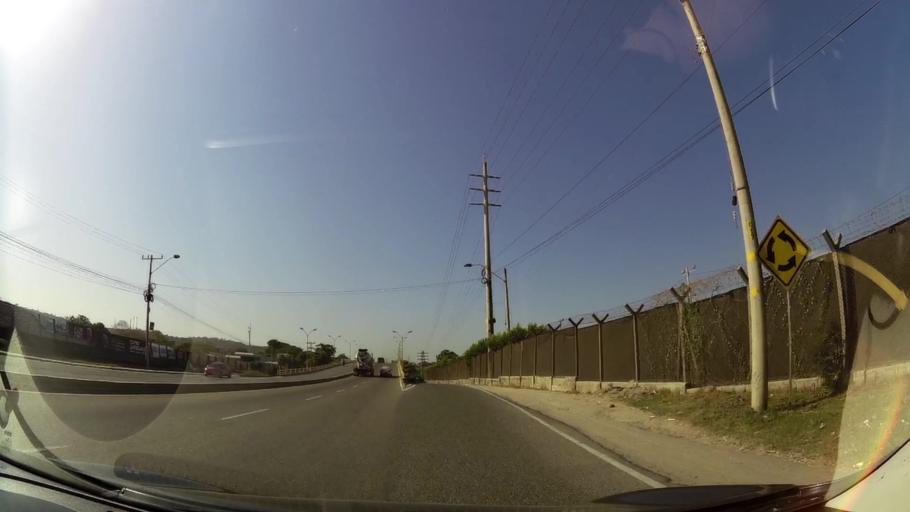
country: CO
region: Bolivar
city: Cartagena
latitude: 10.3746
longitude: -75.5047
